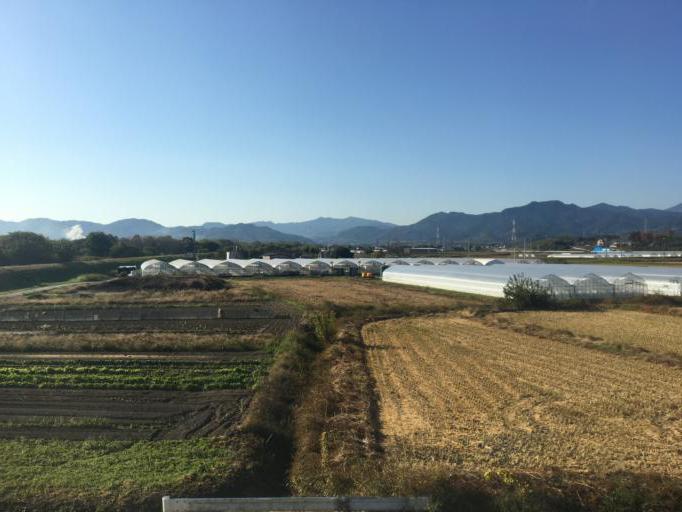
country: JP
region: Gunma
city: Fujioka
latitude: 36.2265
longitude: 139.0846
